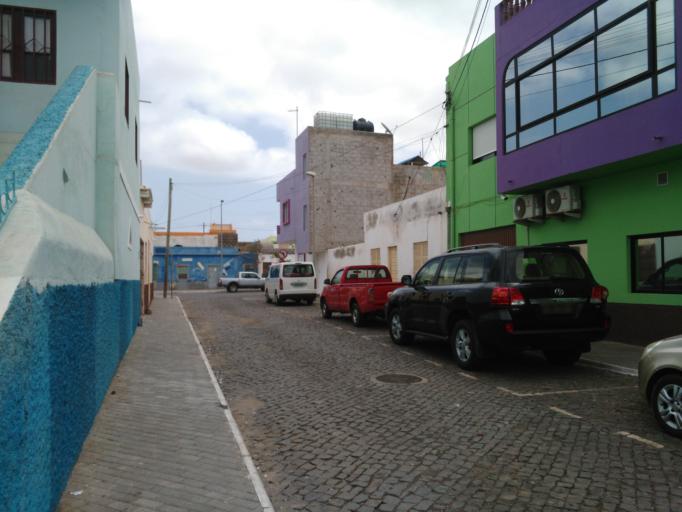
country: CV
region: Sal
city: Espargos
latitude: 16.7545
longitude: -22.9450
